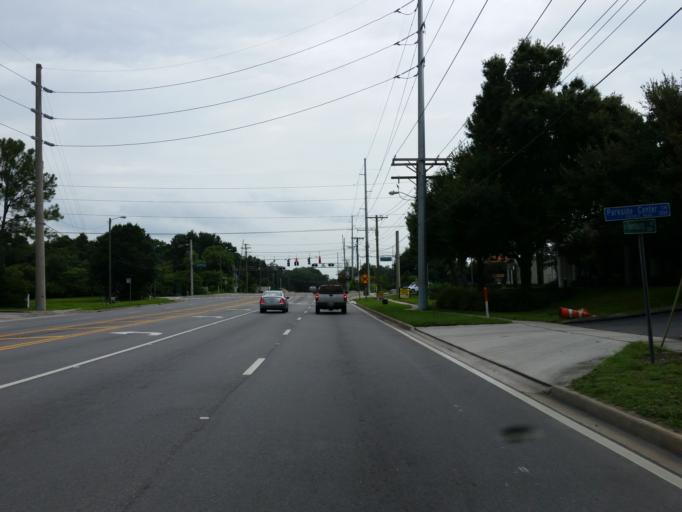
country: US
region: Florida
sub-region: Hillsborough County
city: Mango
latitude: 27.9738
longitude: -82.3352
